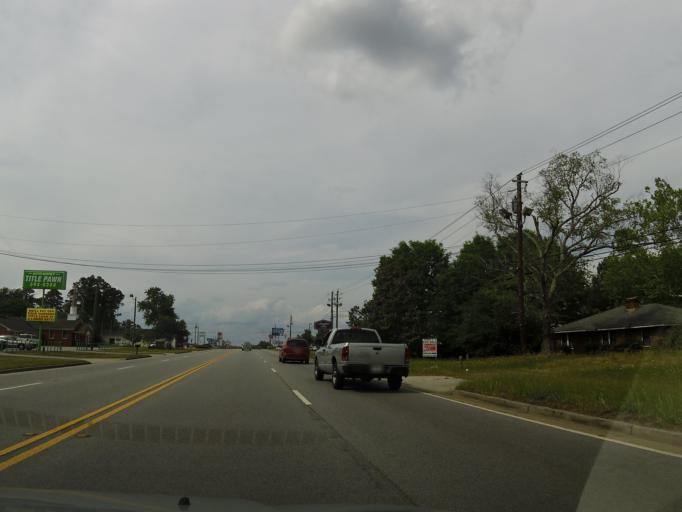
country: US
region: Georgia
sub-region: McDuffie County
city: Thomson
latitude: 33.5015
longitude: -82.5034
